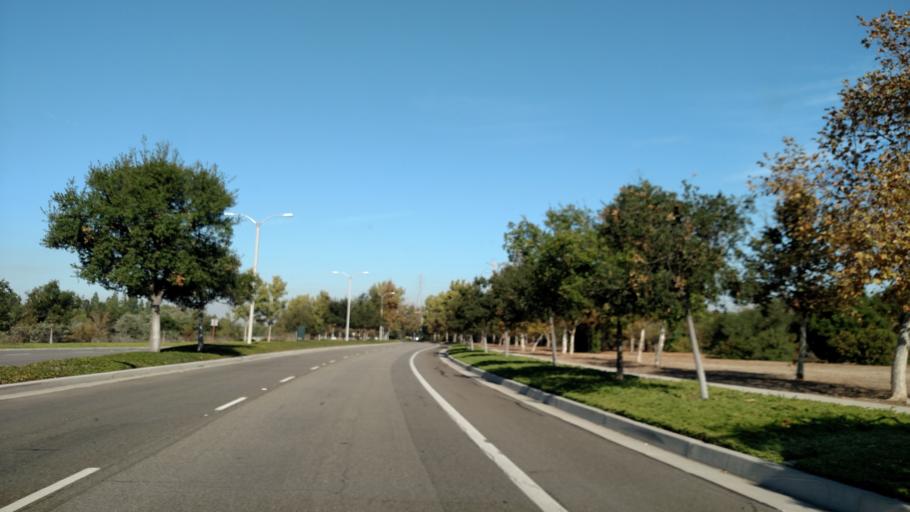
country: US
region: California
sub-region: Orange County
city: Irvine
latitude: 33.6651
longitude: -117.7716
